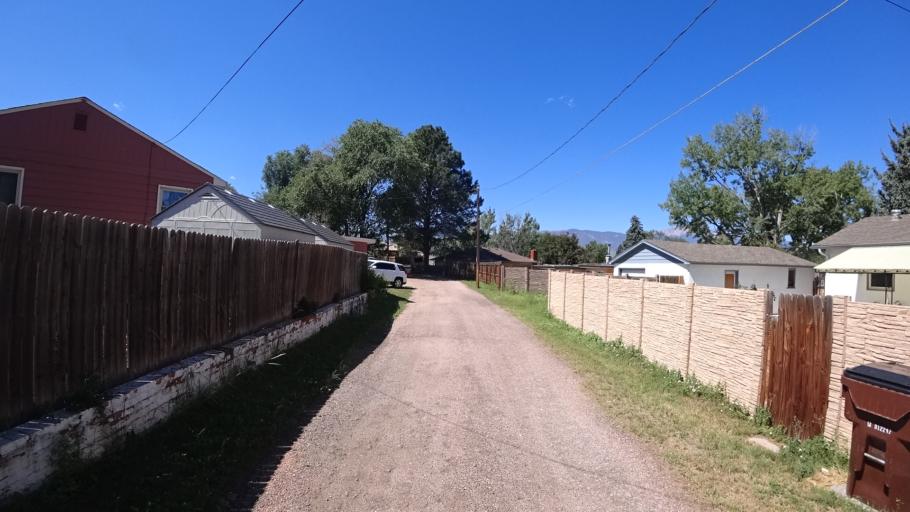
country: US
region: Colorado
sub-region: El Paso County
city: Colorado Springs
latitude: 38.8523
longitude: -104.7945
